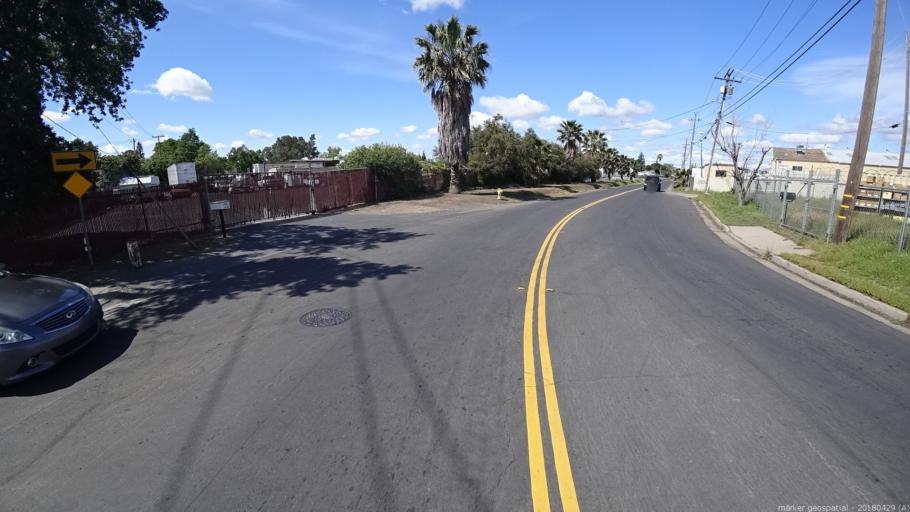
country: US
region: California
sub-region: Yolo County
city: West Sacramento
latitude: 38.5863
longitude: -121.5418
